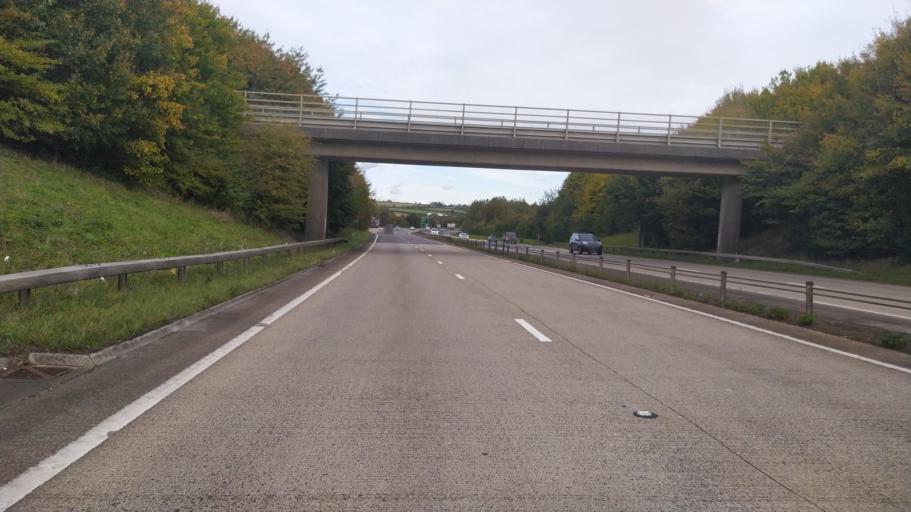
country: GB
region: England
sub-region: Dorset
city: Dorchester
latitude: 50.7488
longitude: -2.3576
